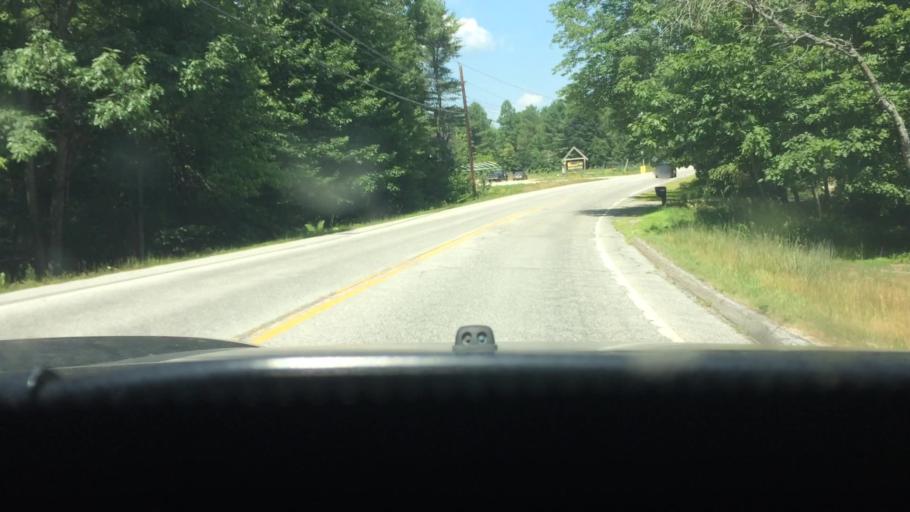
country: US
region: Maine
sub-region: Androscoggin County
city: Mechanic Falls
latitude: 44.1115
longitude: -70.4215
